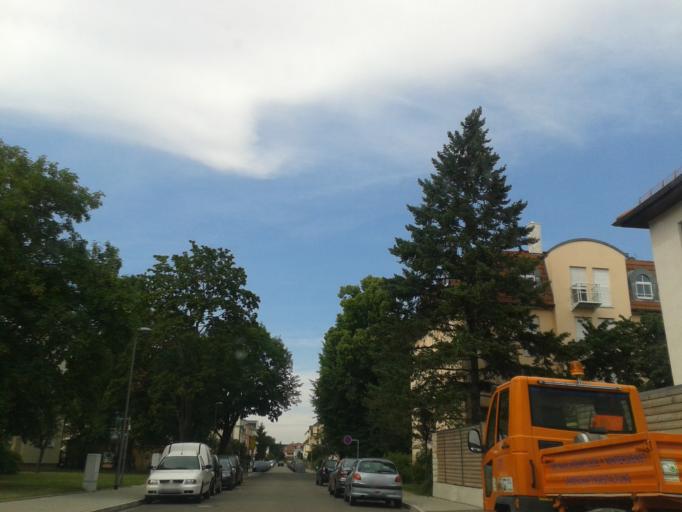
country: DE
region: Saxony
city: Dresden
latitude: 51.0703
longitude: 13.6950
